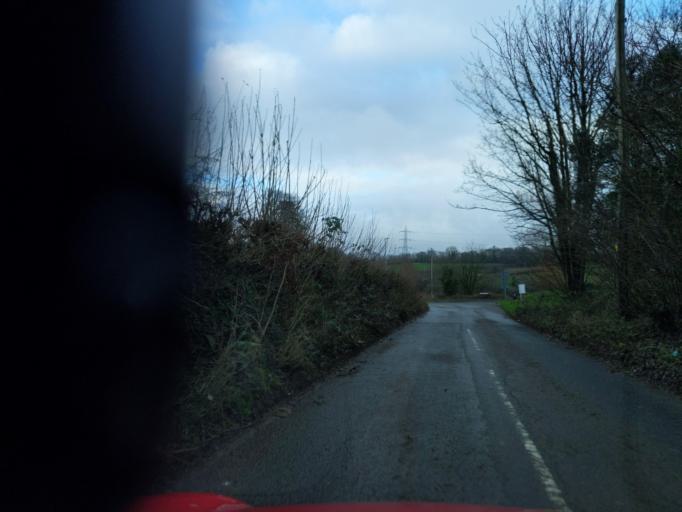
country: GB
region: England
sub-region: Devon
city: Yelverton
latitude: 50.4471
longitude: -4.1191
